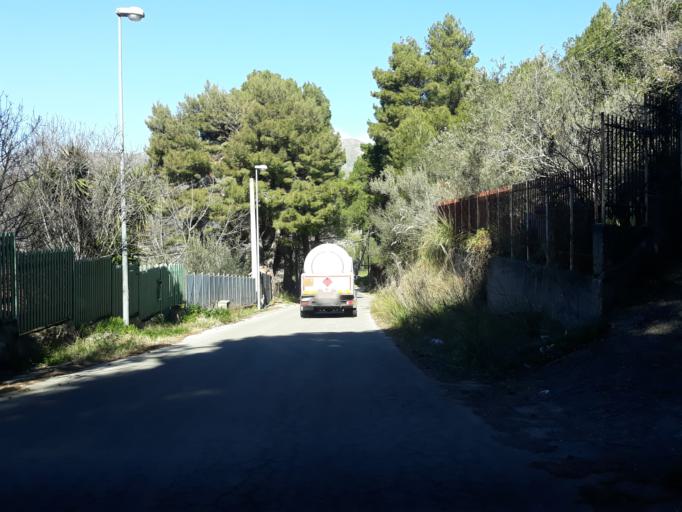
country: IT
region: Sicily
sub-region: Palermo
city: Piano dei Geli
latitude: 38.0830
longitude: 13.2706
